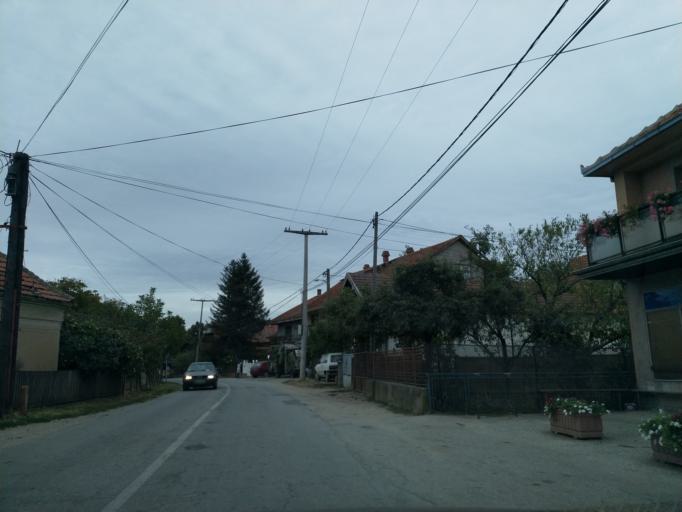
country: RS
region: Central Serbia
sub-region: Pomoravski Okrug
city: Paracin
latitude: 43.8386
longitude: 21.3201
